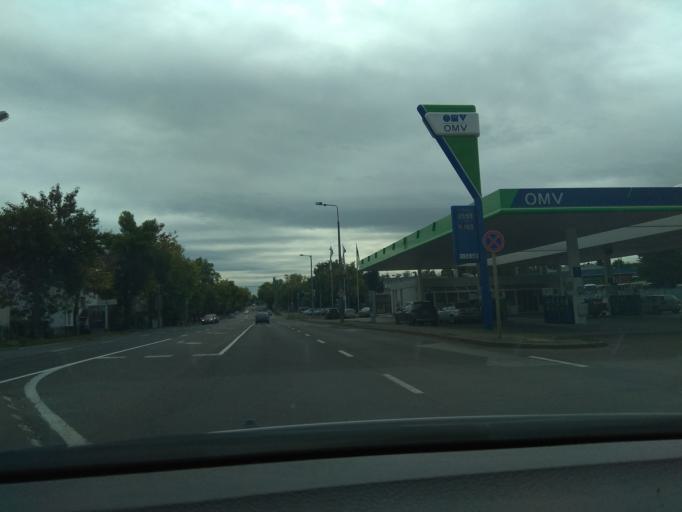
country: HU
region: Heves
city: Eger
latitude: 47.8765
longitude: 20.3822
